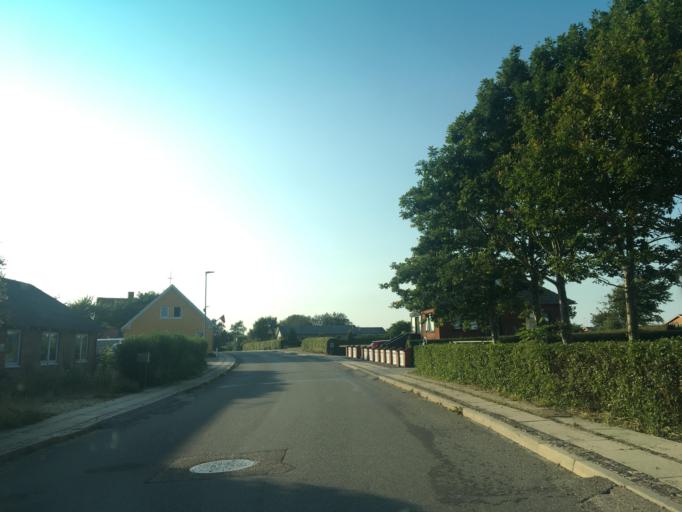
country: DK
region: North Denmark
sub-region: Thisted Kommune
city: Hurup
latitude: 56.8098
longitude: 8.4035
